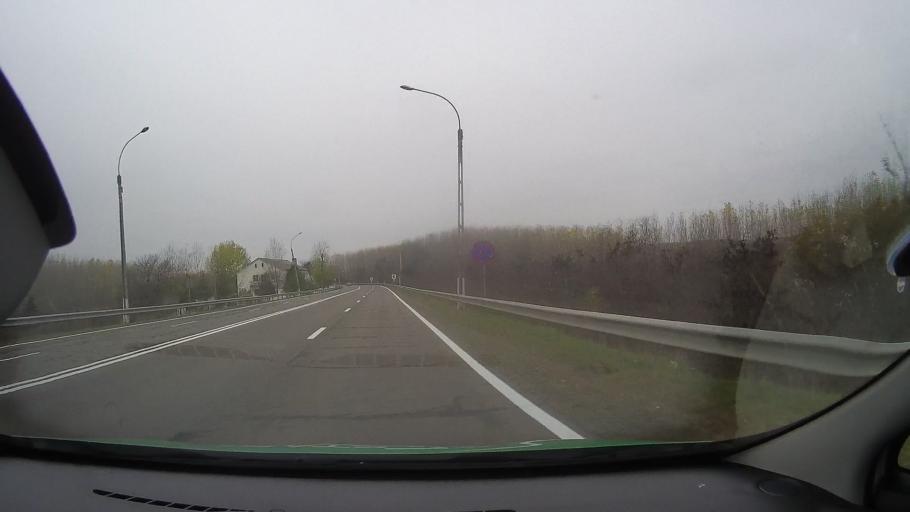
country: RO
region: Ialomita
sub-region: Comuna Giurgeni
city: Giurgeni
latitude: 44.7558
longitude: 27.8668
